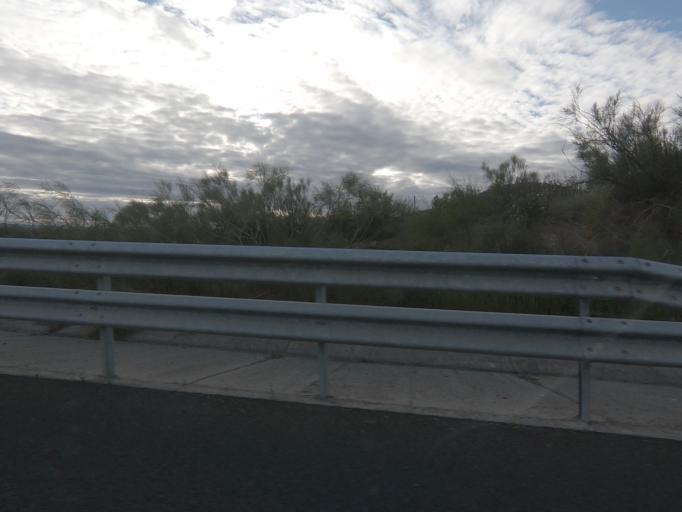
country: ES
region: Extremadura
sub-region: Provincia de Caceres
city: Canaveral
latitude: 39.7881
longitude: -6.3688
